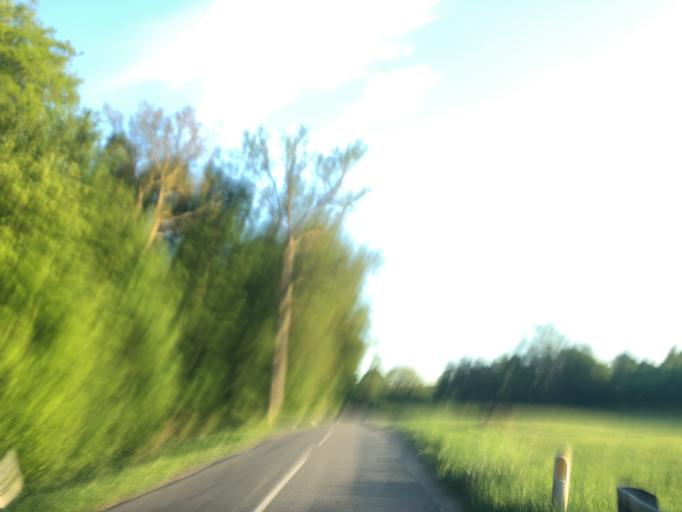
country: DK
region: Zealand
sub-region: Koge Kommune
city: Borup
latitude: 55.4256
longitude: 11.9394
